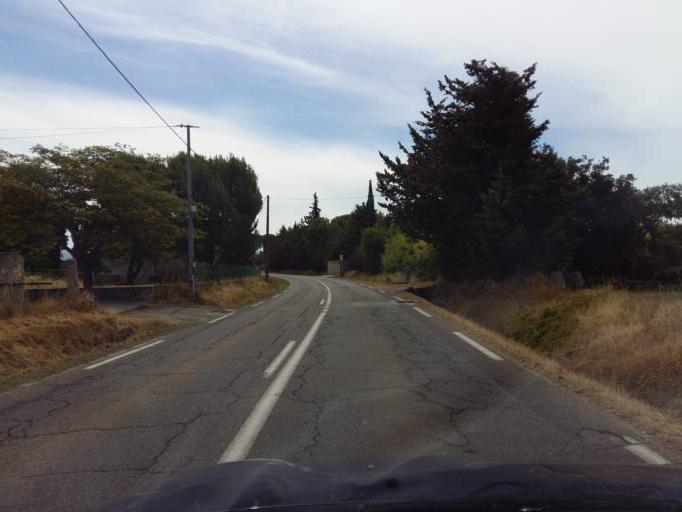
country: FR
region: Provence-Alpes-Cote d'Azur
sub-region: Departement du Vaucluse
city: Carpentras
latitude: 44.0363
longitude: 5.0692
